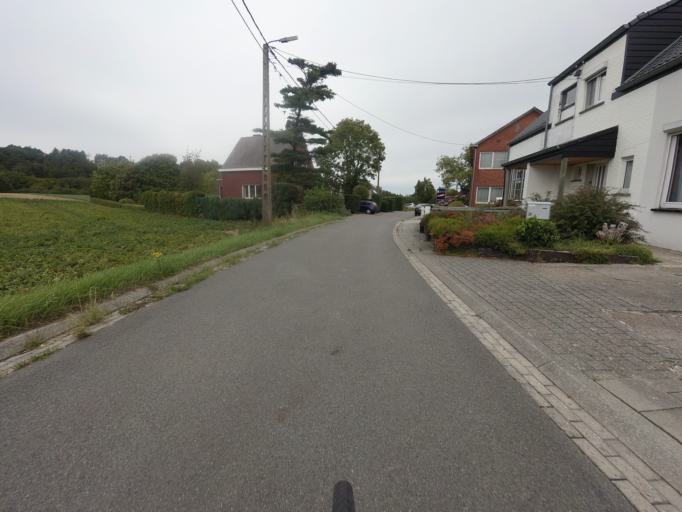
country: BE
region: Flanders
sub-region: Provincie Vlaams-Brabant
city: Leuven
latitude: 50.8956
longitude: 4.6961
